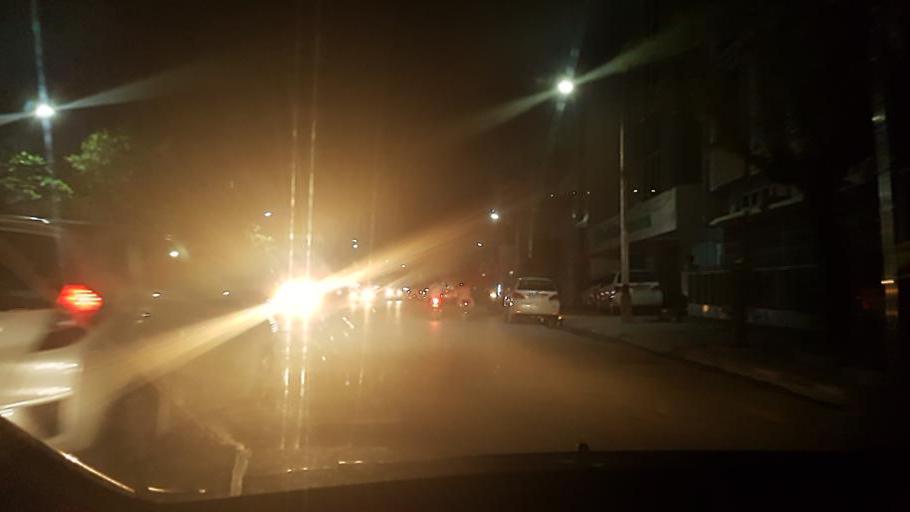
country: MM
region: Mandalay
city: Mandalay
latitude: 21.9727
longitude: 96.0954
